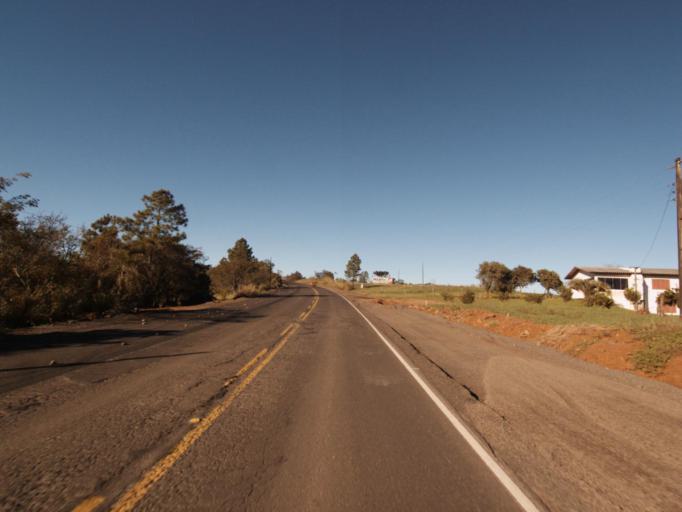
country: AR
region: Misiones
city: Bernardo de Irigoyen
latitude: -26.6468
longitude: -53.5193
